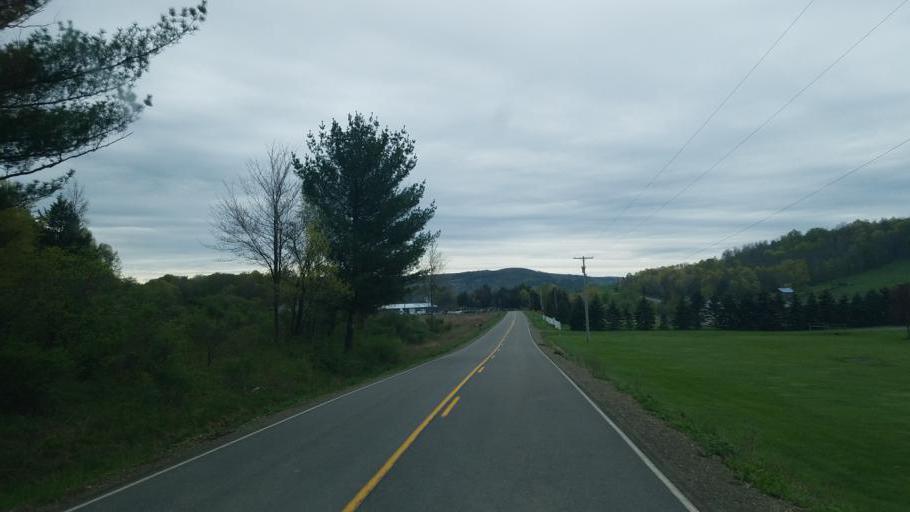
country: US
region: Pennsylvania
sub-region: Tioga County
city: Westfield
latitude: 42.0109
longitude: -77.4766
